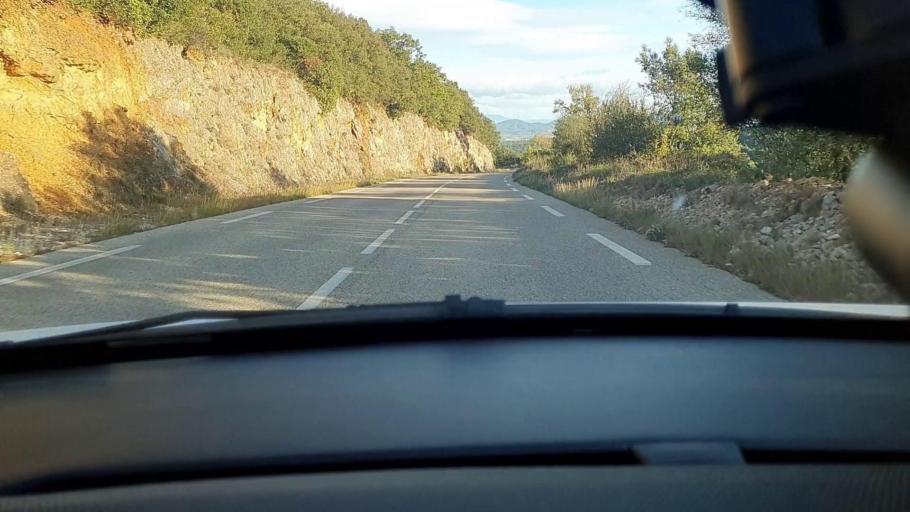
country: FR
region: Languedoc-Roussillon
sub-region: Departement du Gard
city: Barjac
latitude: 44.2291
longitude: 4.3141
